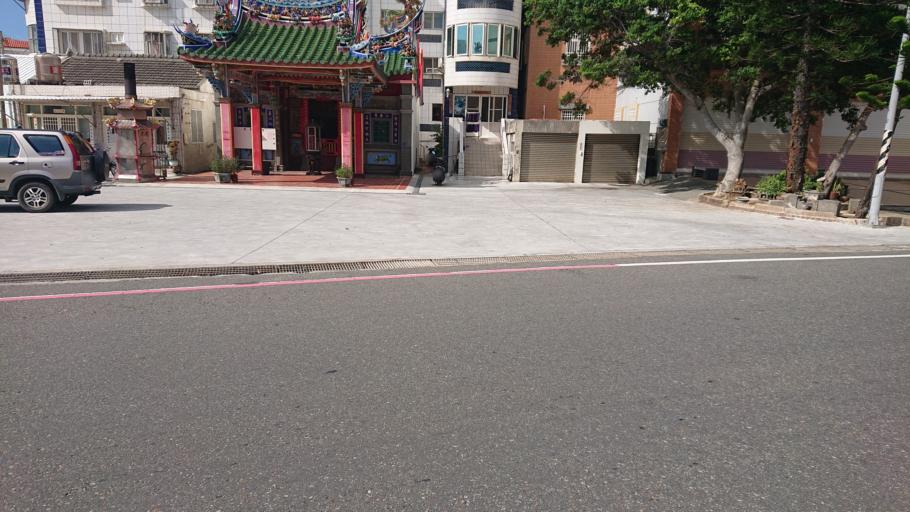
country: TW
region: Taiwan
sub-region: Penghu
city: Ma-kung
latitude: 23.5648
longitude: 119.5844
